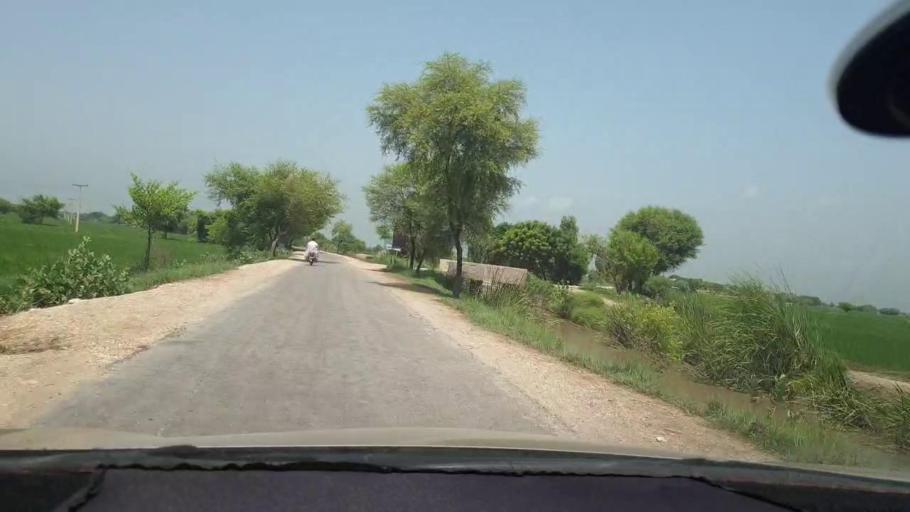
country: PK
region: Sindh
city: Kambar
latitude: 27.6428
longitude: 67.9731
